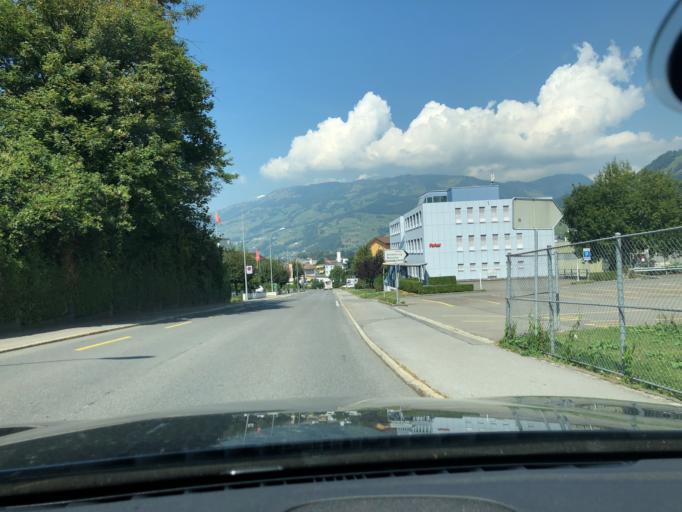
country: CH
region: Schwyz
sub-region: Bezirk Schwyz
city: Ibach
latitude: 47.0234
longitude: 8.6389
